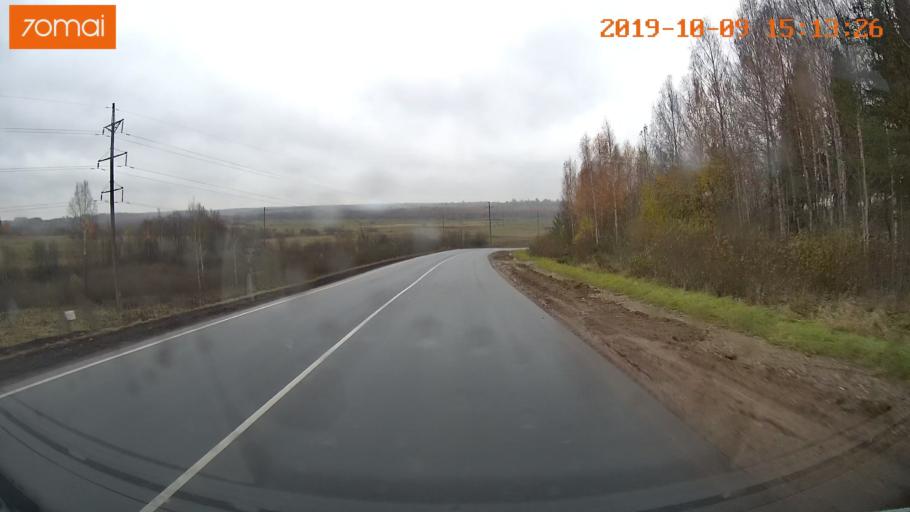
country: RU
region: Kostroma
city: Susanino
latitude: 58.1460
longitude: 41.6151
